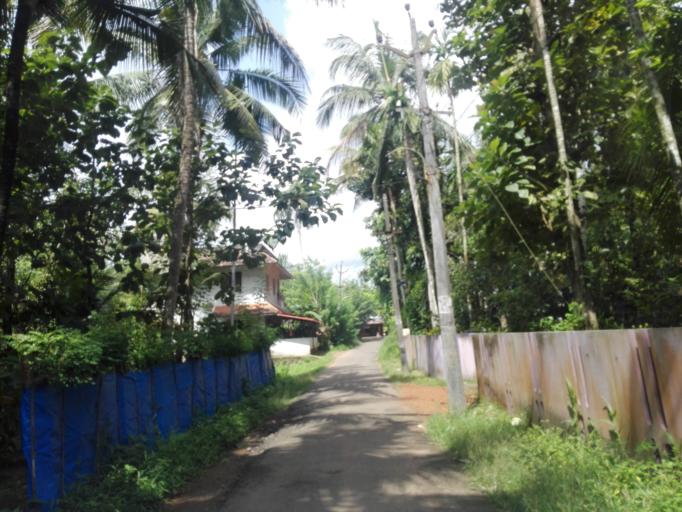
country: IN
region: Kerala
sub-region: Alappuzha
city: Arukutti
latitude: 9.8303
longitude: 76.3903
